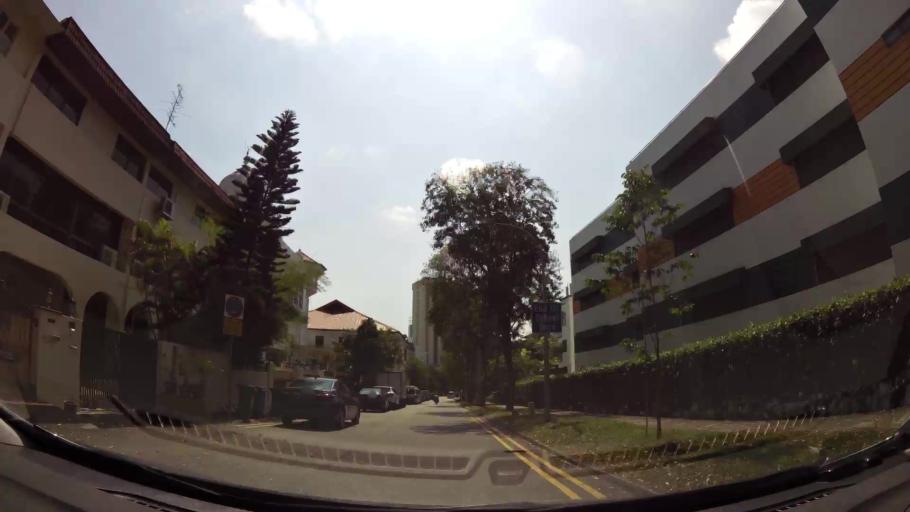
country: SG
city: Singapore
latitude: 1.3044
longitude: 103.8465
